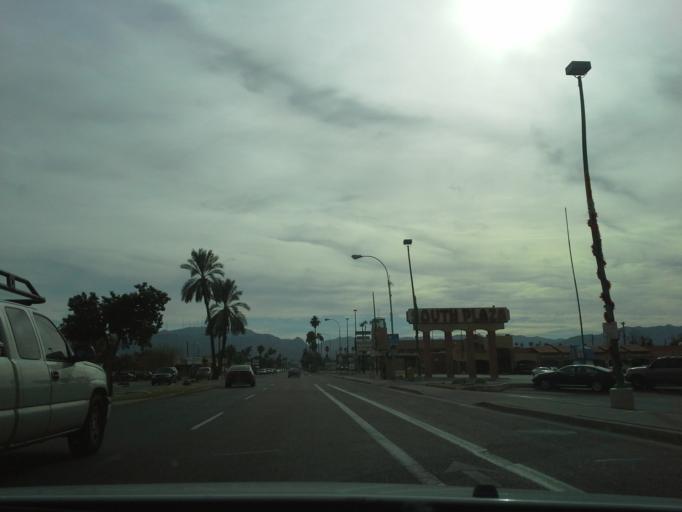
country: US
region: Arizona
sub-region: Maricopa County
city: Phoenix
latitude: 33.3920
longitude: -112.0734
